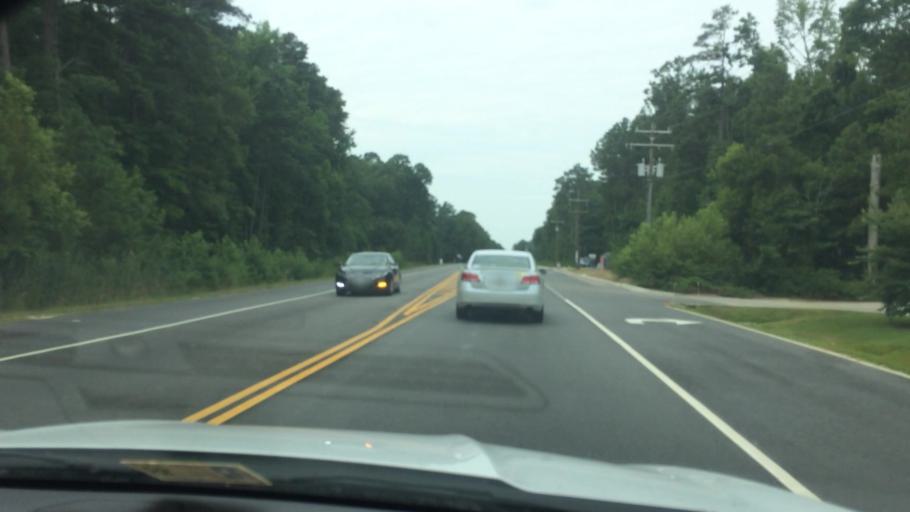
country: US
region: Virginia
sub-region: York County
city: Yorktown
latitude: 37.1565
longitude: -76.5040
